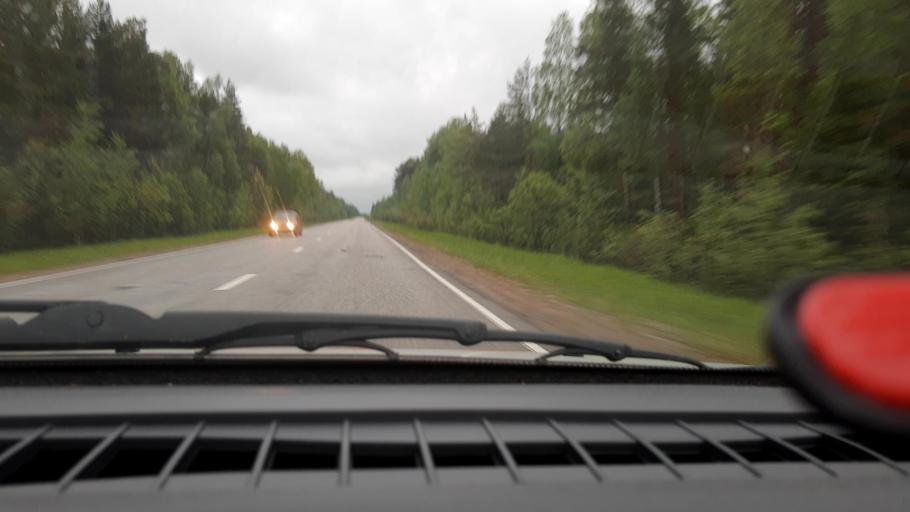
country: RU
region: Nizjnij Novgorod
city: Krasnyye Baki
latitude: 57.1850
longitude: 45.3937
